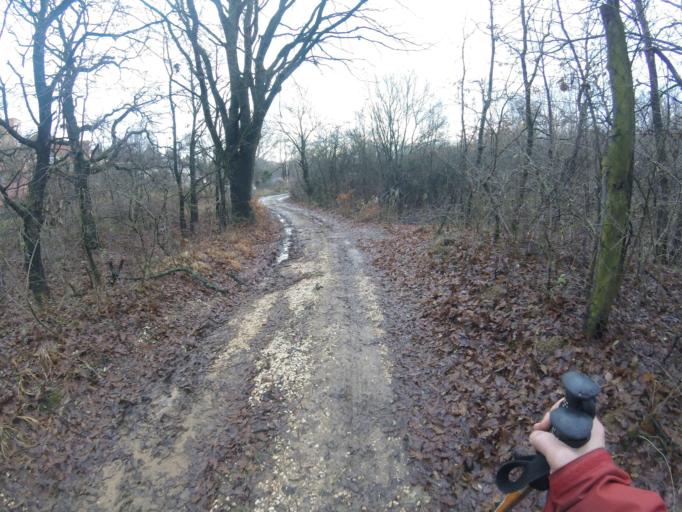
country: HU
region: Pest
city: Budakeszi
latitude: 47.5230
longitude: 18.9162
